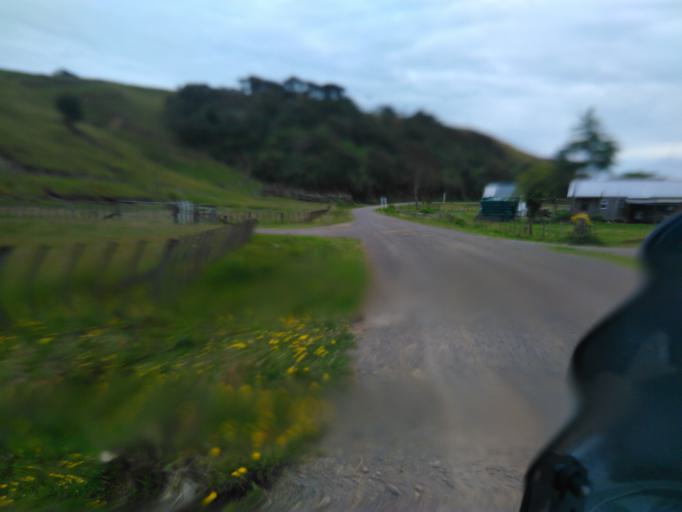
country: NZ
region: Bay of Plenty
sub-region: Opotiki District
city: Opotiki
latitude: -38.0241
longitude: 177.4369
